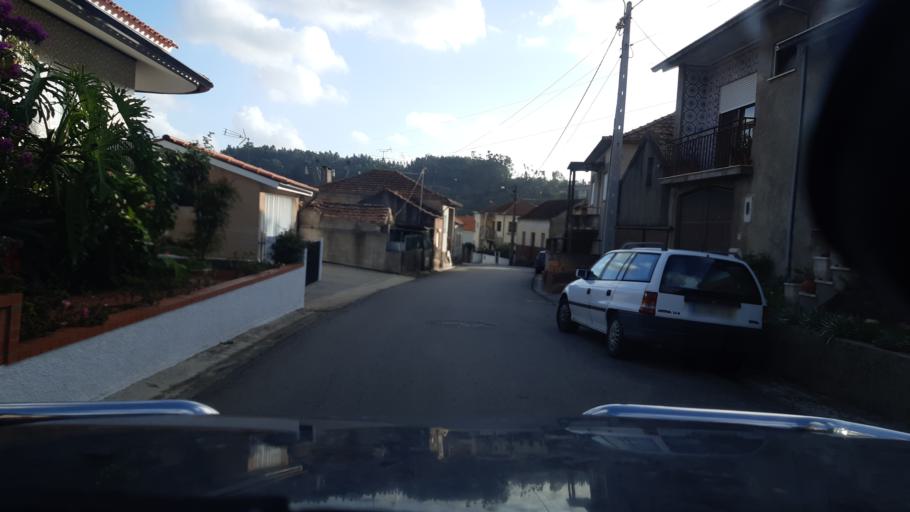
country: PT
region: Aveiro
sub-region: Agueda
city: Agueda
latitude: 40.5734
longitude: -8.4708
